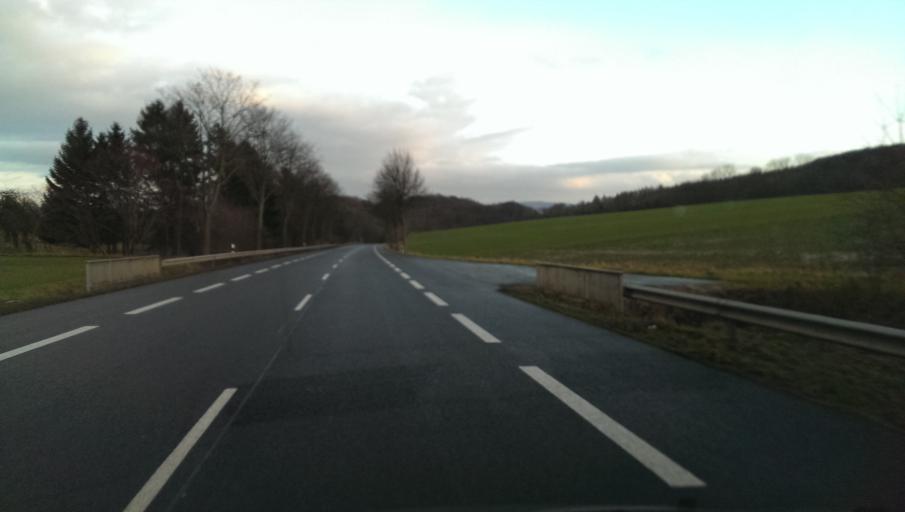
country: DE
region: Lower Saxony
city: Kreiensen
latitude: 51.8632
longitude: 9.9140
